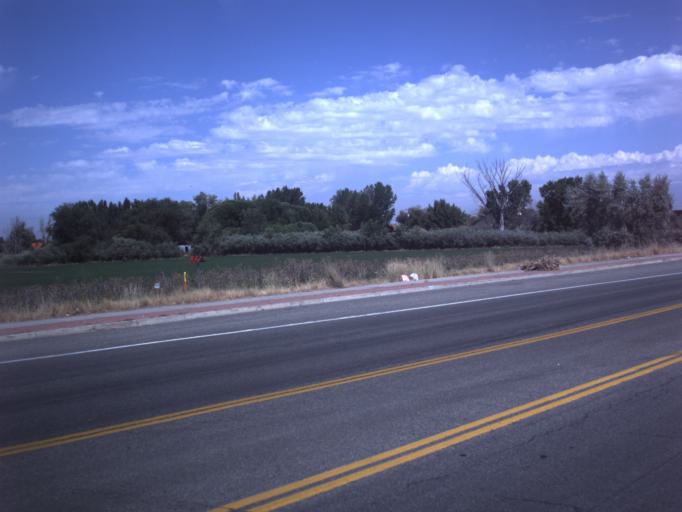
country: US
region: Utah
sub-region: Weber County
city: Marriott-Slaterville
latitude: 41.2481
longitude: -112.0252
